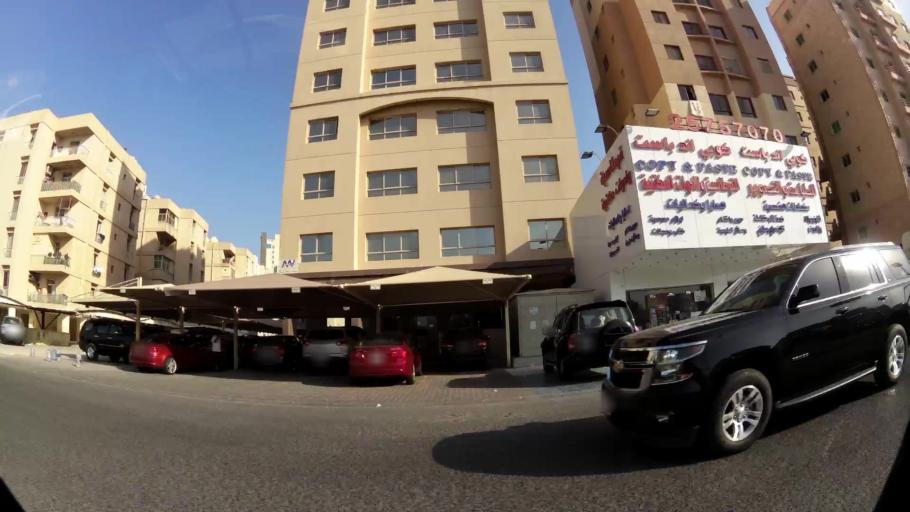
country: KW
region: Muhafazat Hawalli
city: As Salimiyah
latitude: 29.3408
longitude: 48.0918
